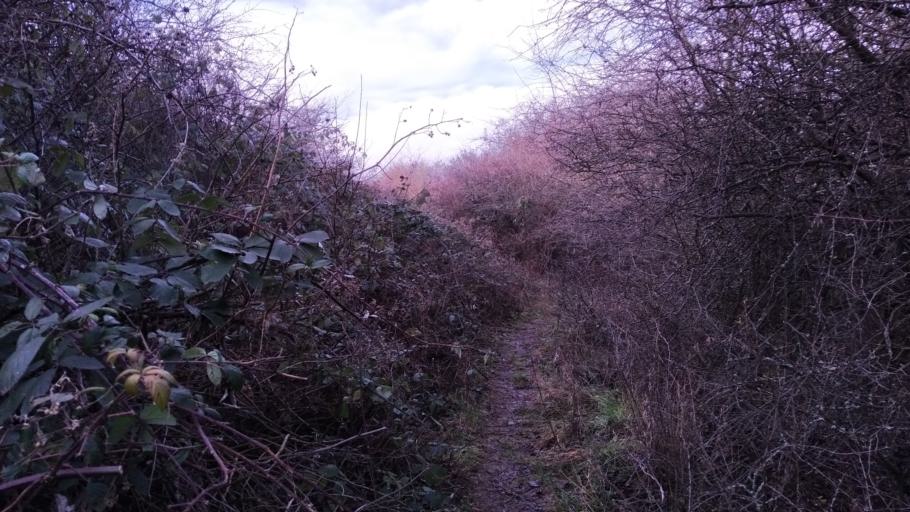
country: HU
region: Pest
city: Pomaz
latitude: 47.6227
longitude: 19.0160
